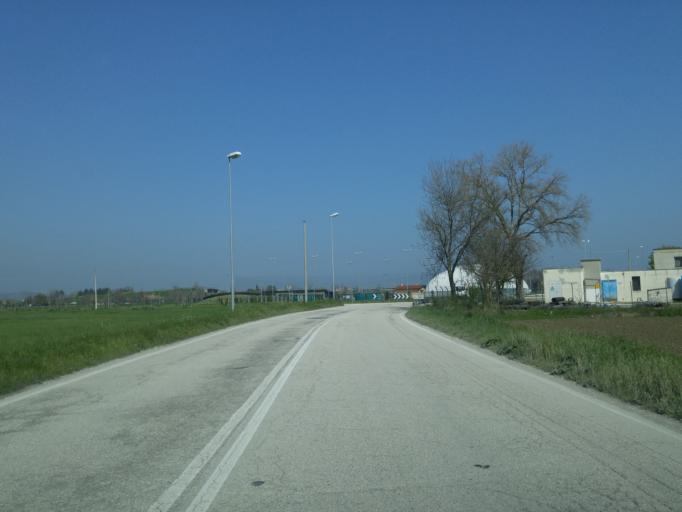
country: IT
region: The Marches
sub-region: Provincia di Pesaro e Urbino
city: Rosciano
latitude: 43.8093
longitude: 13.0142
